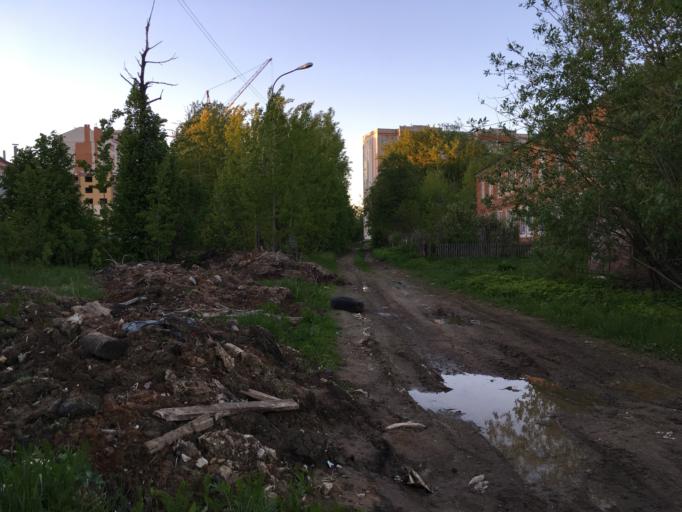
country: RU
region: Mariy-El
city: Yoshkar-Ola
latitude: 56.6318
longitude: 47.9351
